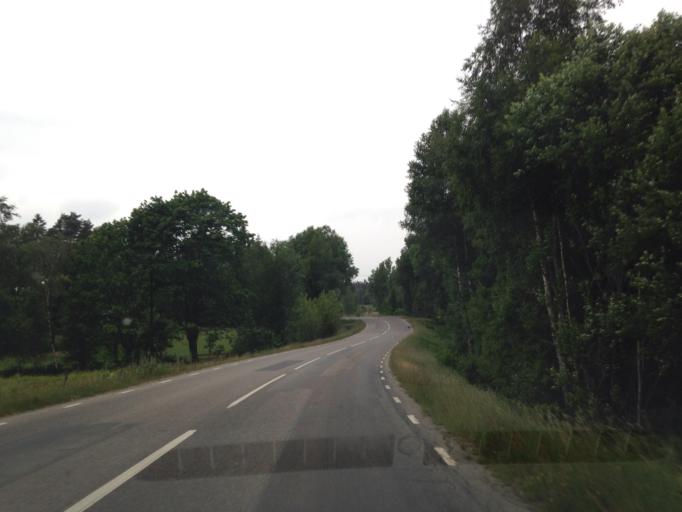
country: SE
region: Vaestra Goetaland
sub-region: Lerums Kommun
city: Lerum
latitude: 57.6757
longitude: 12.3343
